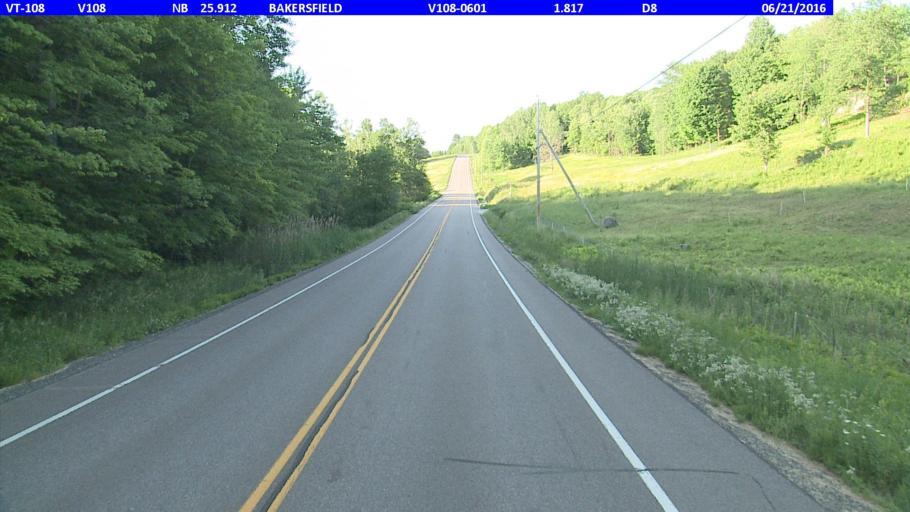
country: US
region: Vermont
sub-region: Franklin County
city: Enosburg Falls
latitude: 44.7585
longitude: -72.8184
